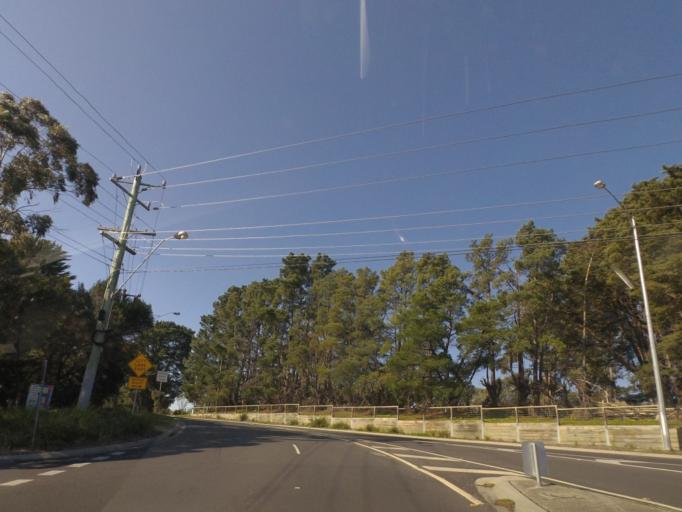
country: AU
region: Victoria
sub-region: Manningham
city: Donvale
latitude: -37.7839
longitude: 145.1817
